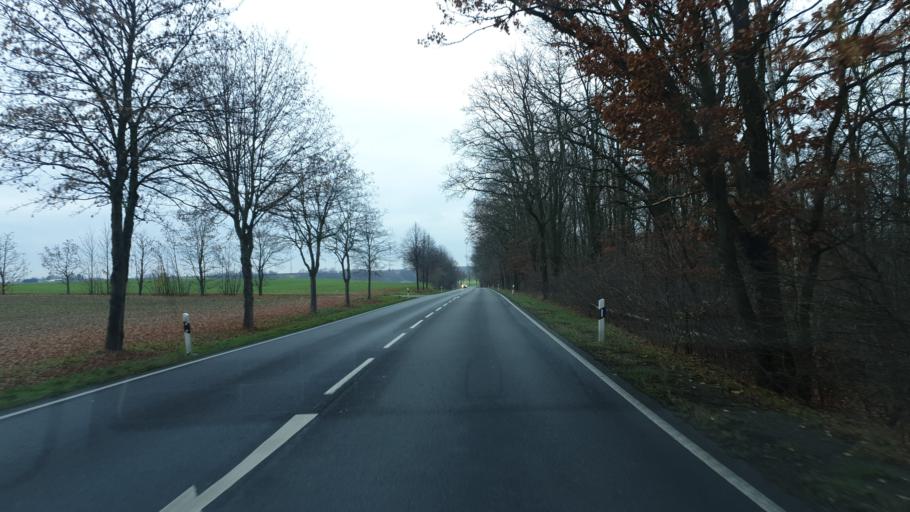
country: DE
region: Saxony-Anhalt
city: Stossen
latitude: 51.1254
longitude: 11.9001
